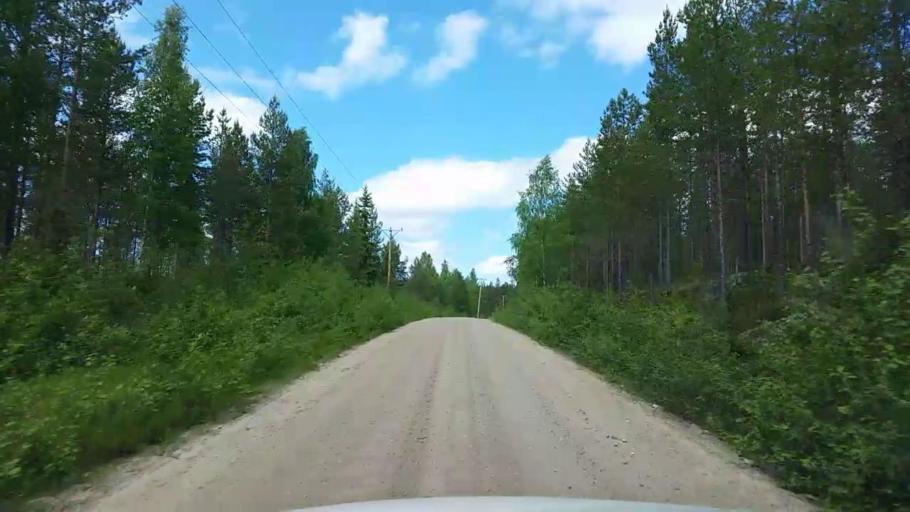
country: SE
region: Gaevleborg
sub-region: Ovanakers Kommun
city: Alfta
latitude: 61.5528
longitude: 15.9705
